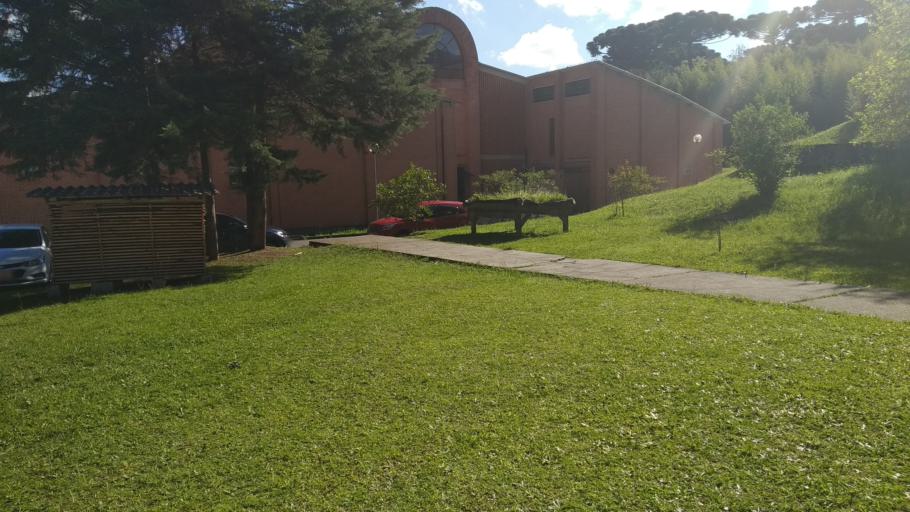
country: BR
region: Parana
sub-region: Curitiba
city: Curitiba
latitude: -25.4483
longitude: -49.2376
